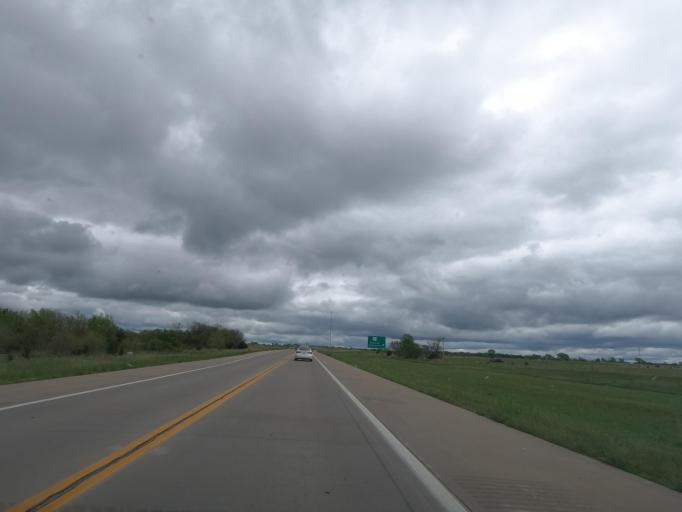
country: US
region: Kansas
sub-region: Montgomery County
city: Cherryvale
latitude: 37.3468
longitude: -95.5412
